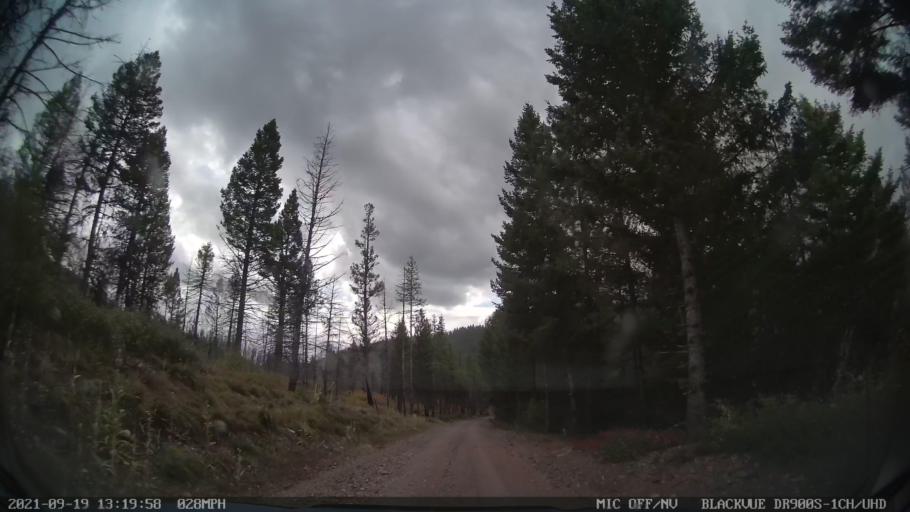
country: US
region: Montana
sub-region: Missoula County
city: Seeley Lake
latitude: 47.1671
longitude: -113.3455
